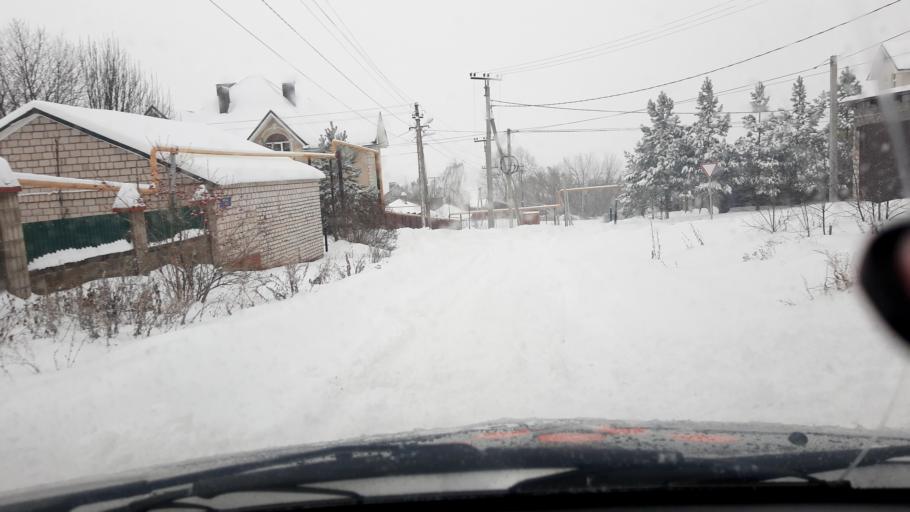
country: RU
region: Bashkortostan
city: Ufa
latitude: 54.6054
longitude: 55.9568
